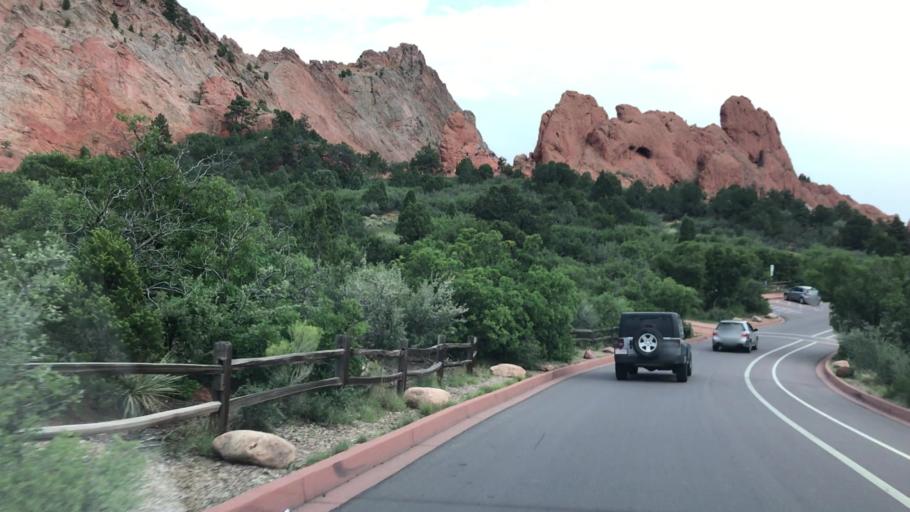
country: US
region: Colorado
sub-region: El Paso County
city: Manitou Springs
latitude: 38.8762
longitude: -104.8828
